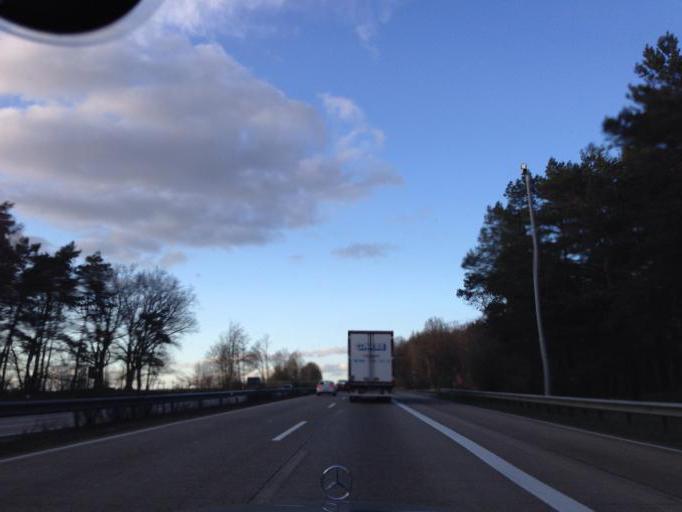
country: DE
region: Lower Saxony
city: Bad Fallingbostel
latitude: 52.8177
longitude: 9.6825
